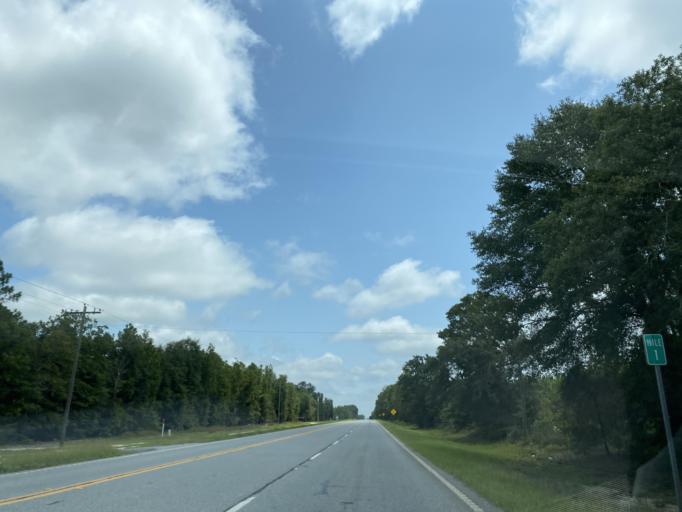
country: US
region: Georgia
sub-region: Telfair County
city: McRae
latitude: 32.0874
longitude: -82.8729
